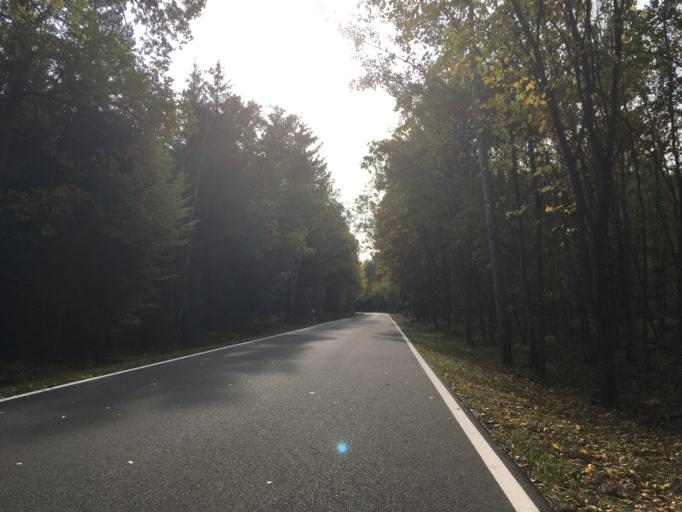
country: DE
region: Brandenburg
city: Templin
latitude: 53.0152
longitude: 13.4664
